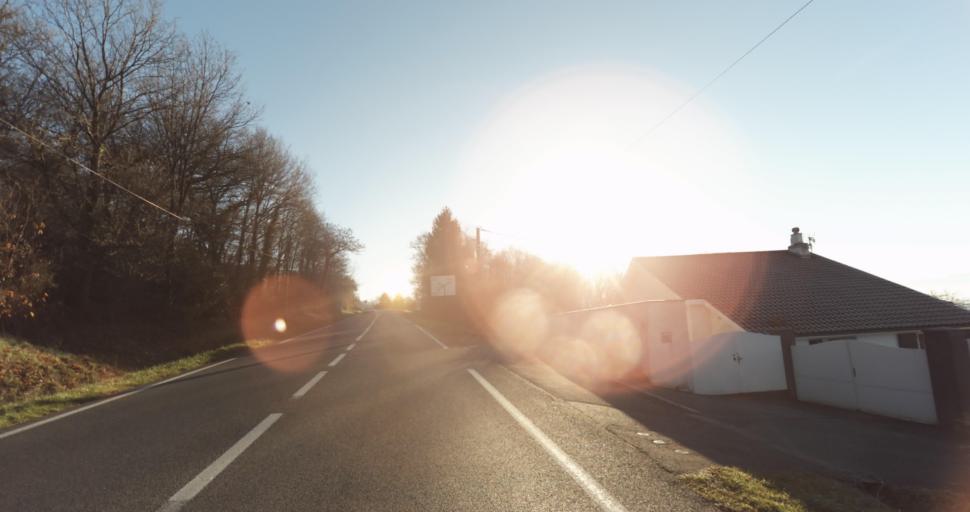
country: FR
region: Aquitaine
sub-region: Departement des Pyrenees-Atlantiques
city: Morlaas
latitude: 43.3311
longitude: -0.2782
